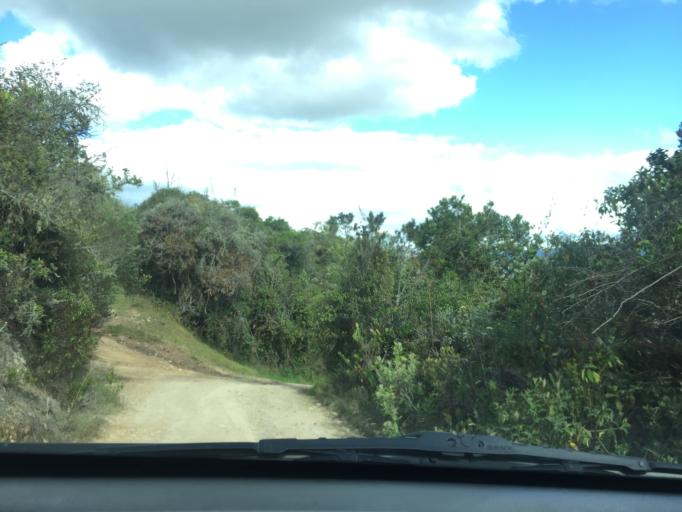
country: CO
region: Cundinamarca
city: Tocancipa
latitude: 4.9329
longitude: -73.8962
